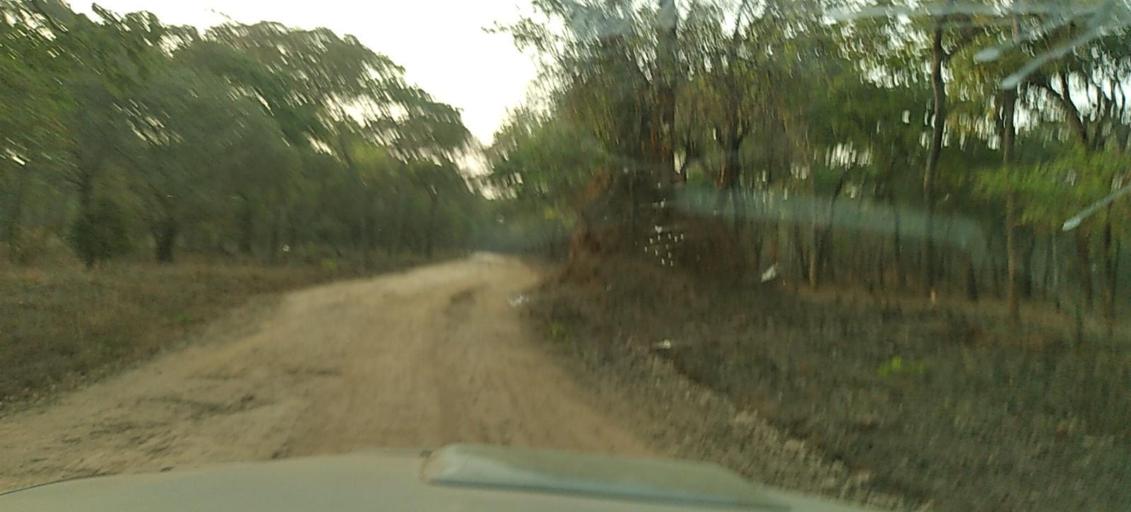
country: ZM
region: North-Western
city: Kasempa
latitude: -13.1590
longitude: 26.4495
